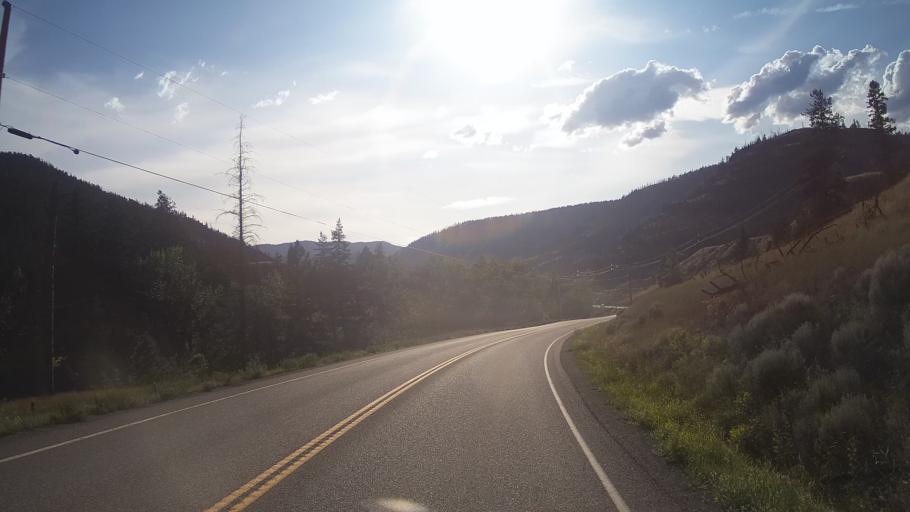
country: CA
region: British Columbia
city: Cache Creek
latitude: 50.8841
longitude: -121.4752
